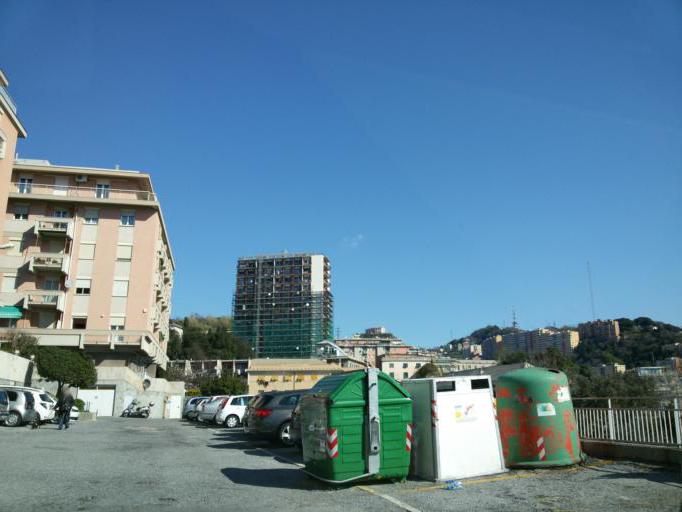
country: IT
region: Liguria
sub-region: Provincia di Genova
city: San Teodoro
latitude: 44.4155
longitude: 8.9068
